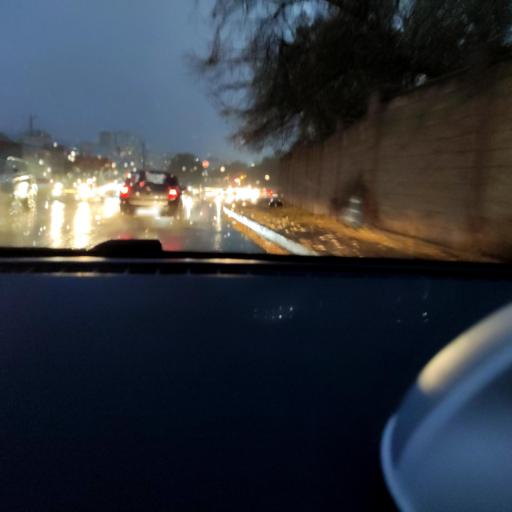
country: RU
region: Samara
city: Petra-Dubrava
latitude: 53.2433
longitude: 50.2724
